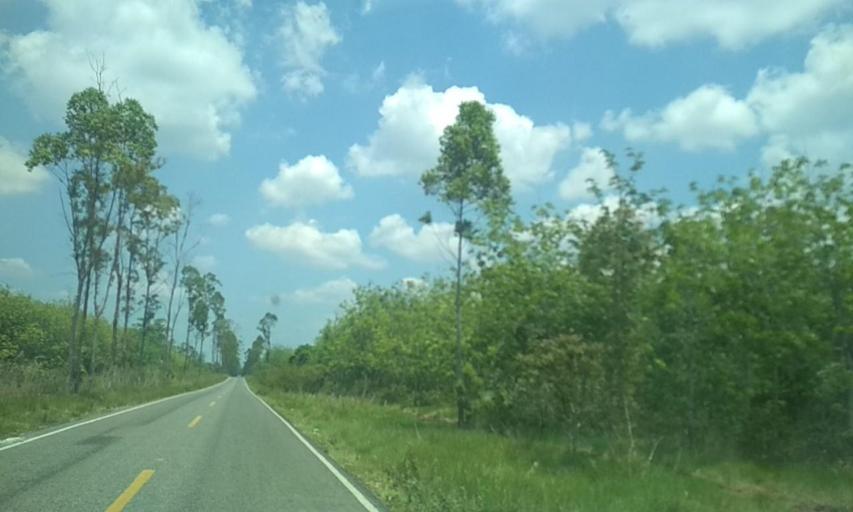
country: MX
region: Tabasco
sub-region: Huimanguillo
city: Huapacal 1ra. Seccion
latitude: 17.7517
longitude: -93.7113
